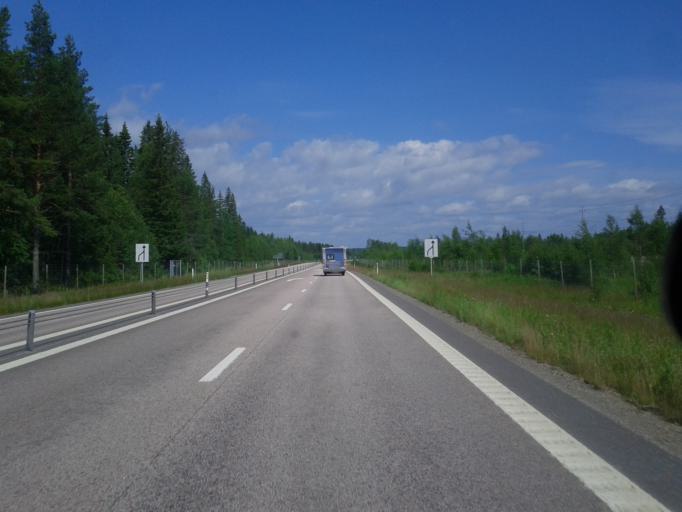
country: SE
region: Vaesterbotten
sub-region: Nordmalings Kommun
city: Nordmaling
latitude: 63.5621
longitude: 19.4283
